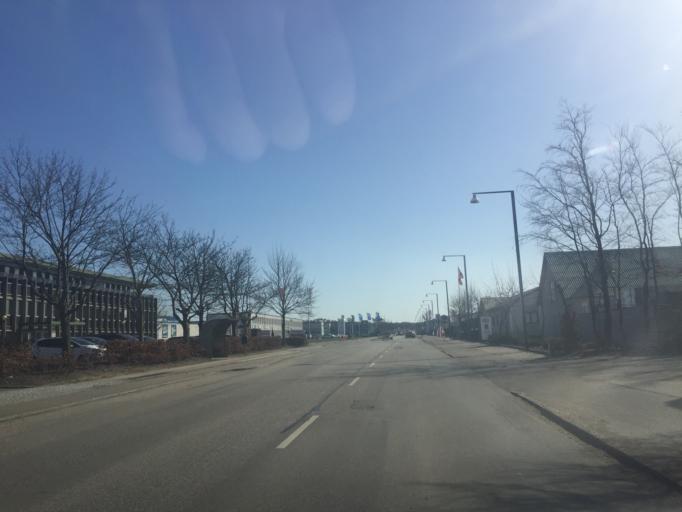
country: DK
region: Capital Region
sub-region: Rodovre Kommune
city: Rodovre
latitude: 55.6964
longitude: 12.4325
